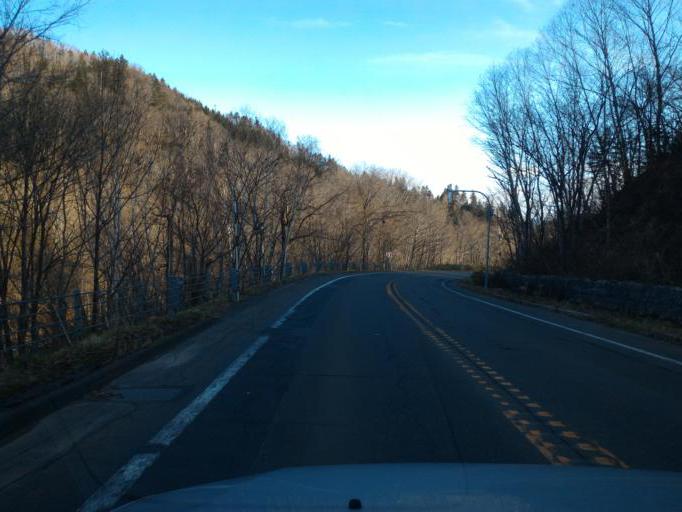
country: JP
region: Hokkaido
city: Utashinai
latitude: 43.2969
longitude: 142.1002
